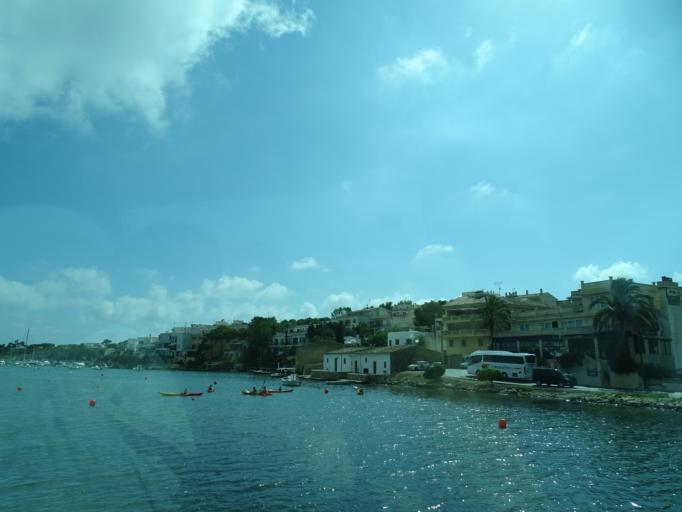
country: ES
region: Balearic Islands
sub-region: Illes Balears
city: Santanyi
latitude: 39.3647
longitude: 3.2114
